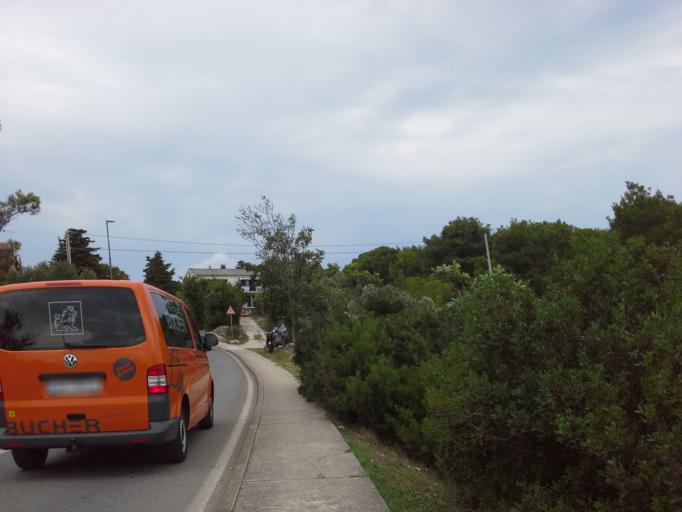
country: HR
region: Primorsko-Goranska
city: Mali Losinj
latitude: 44.5360
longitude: 14.4697
